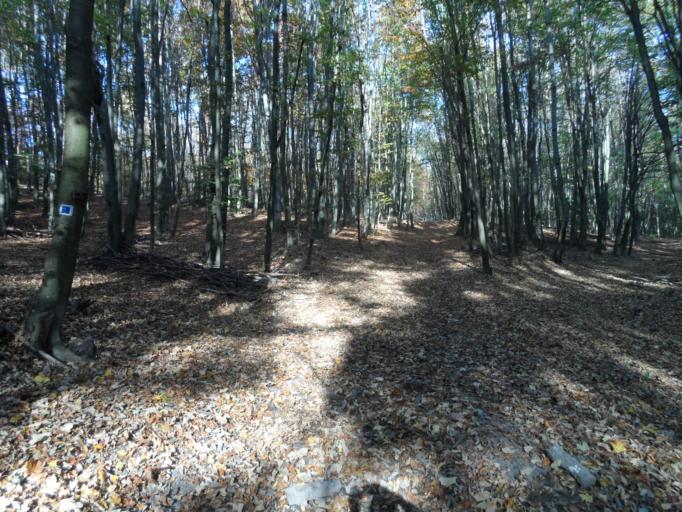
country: HU
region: Veszprem
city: Urkut
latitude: 47.2108
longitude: 17.6398
